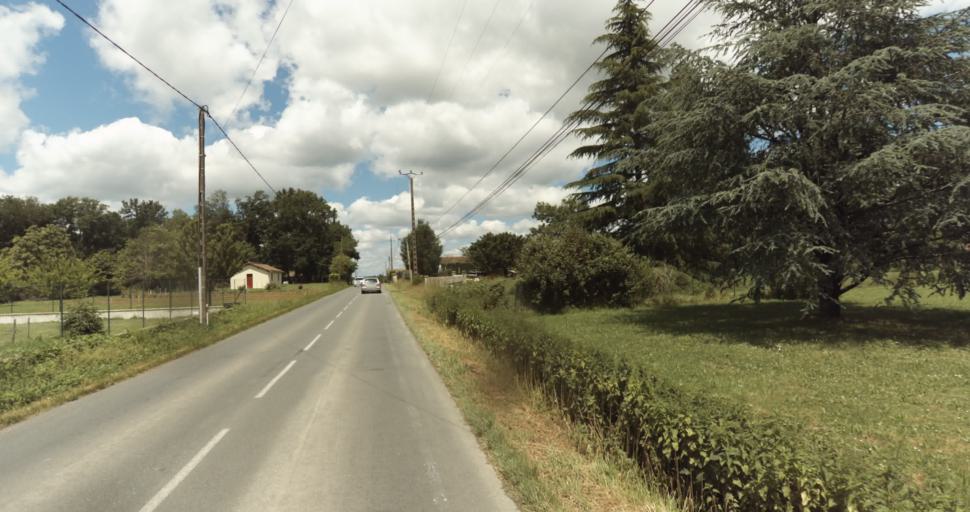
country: FR
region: Aquitaine
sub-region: Departement de la Dordogne
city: Beaumont-du-Perigord
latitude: 44.7321
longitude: 0.7550
